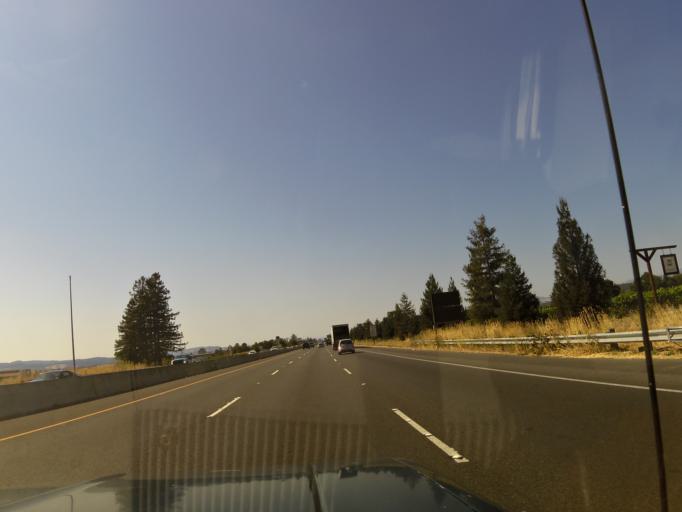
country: US
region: California
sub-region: Sonoma County
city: Larkfield-Wikiup
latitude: 38.5156
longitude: -122.7805
